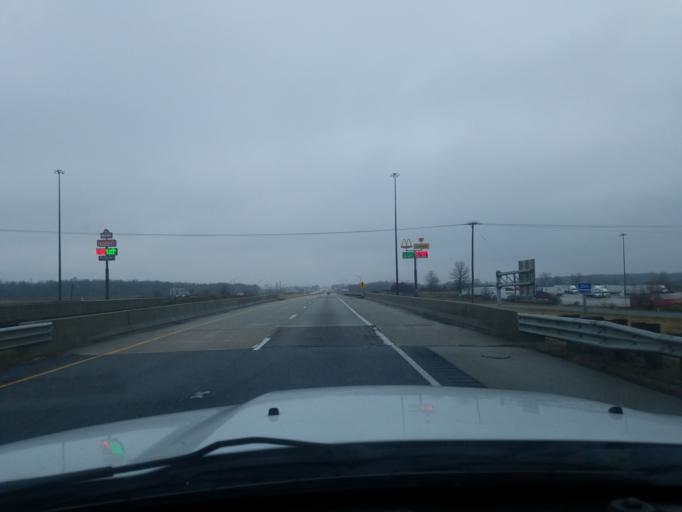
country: US
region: Indiana
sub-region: Grant County
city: Gas City
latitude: 40.5530
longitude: -85.5506
